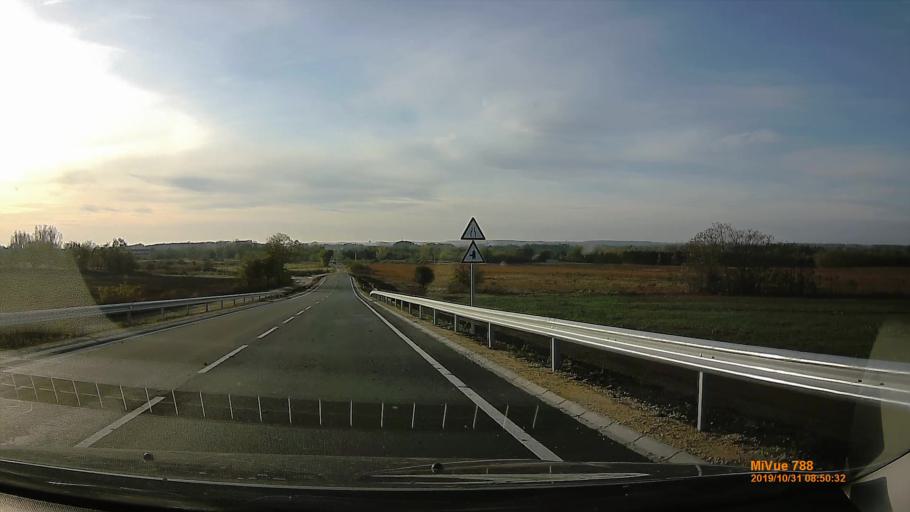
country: HU
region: Pest
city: Albertirsa
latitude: 47.2699
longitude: 19.6044
